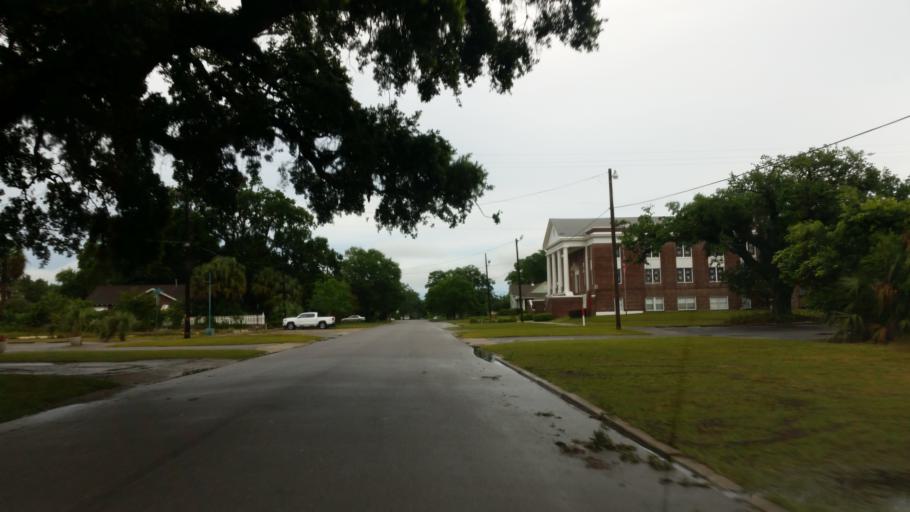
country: US
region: Florida
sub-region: Escambia County
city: Pensacola
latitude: 30.4230
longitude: -87.2018
